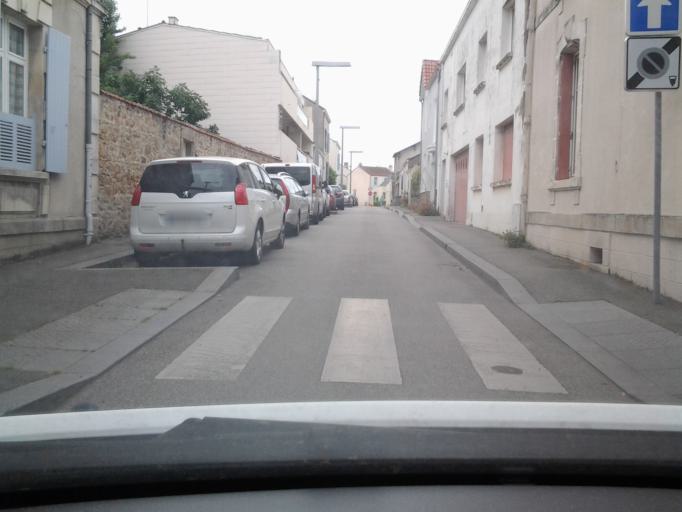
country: FR
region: Pays de la Loire
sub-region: Departement de la Vendee
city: La Roche-sur-Yon
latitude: 46.6676
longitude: -1.4310
